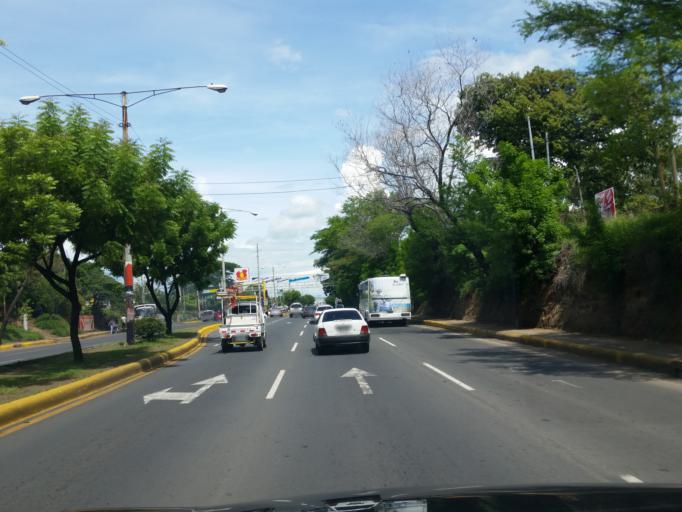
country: NI
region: Managua
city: Managua
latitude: 12.1484
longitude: -86.2008
